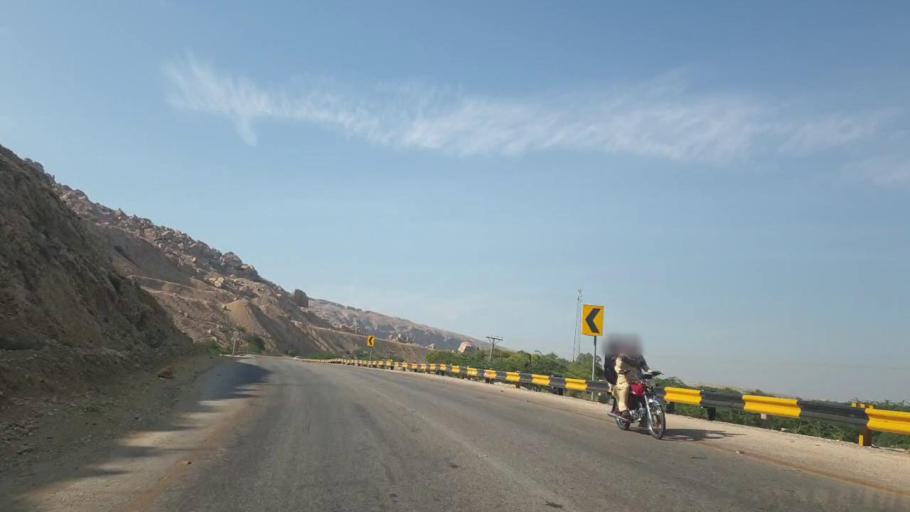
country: PK
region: Sindh
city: Sehwan
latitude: 26.3217
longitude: 67.8869
